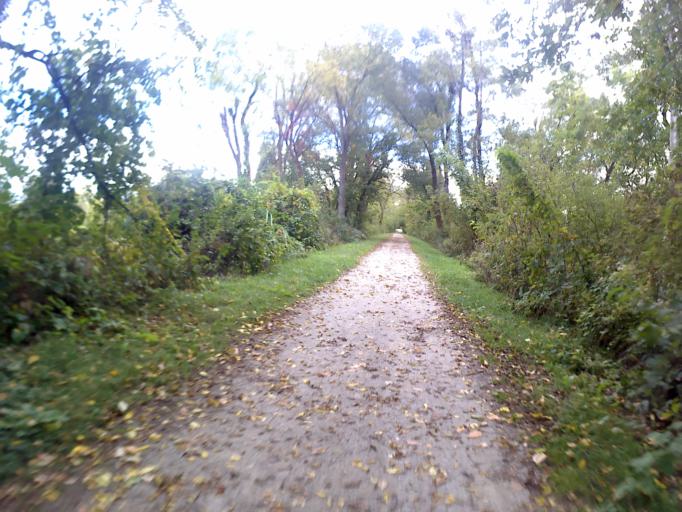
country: US
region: Illinois
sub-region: DuPage County
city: Wayne
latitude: 41.9493
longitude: -88.2397
